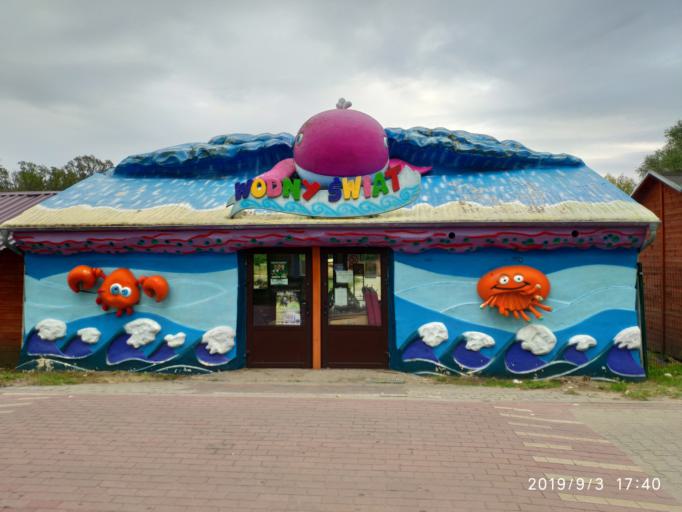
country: PL
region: Lubusz
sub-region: Powiat nowosolski
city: Nowa Sol
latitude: 51.7994
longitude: 15.7252
